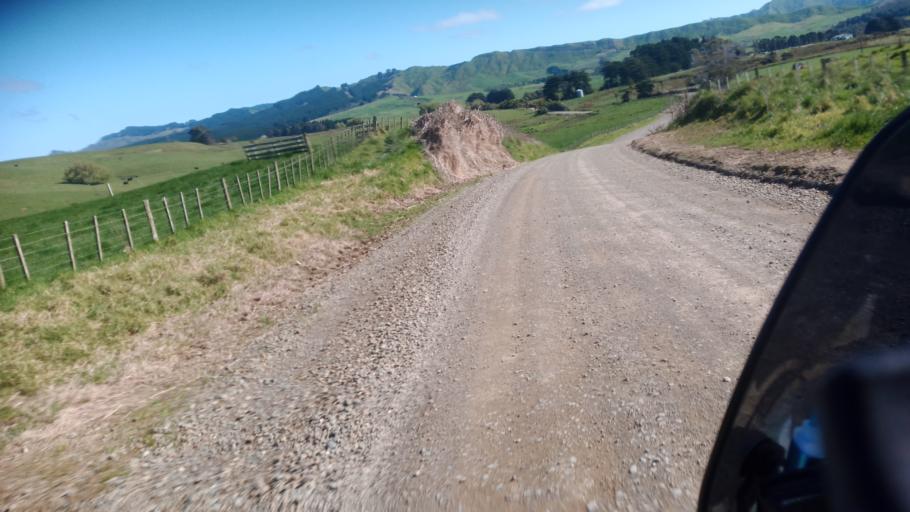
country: NZ
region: Gisborne
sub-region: Gisborne District
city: Gisborne
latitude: -39.1372
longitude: 177.9344
